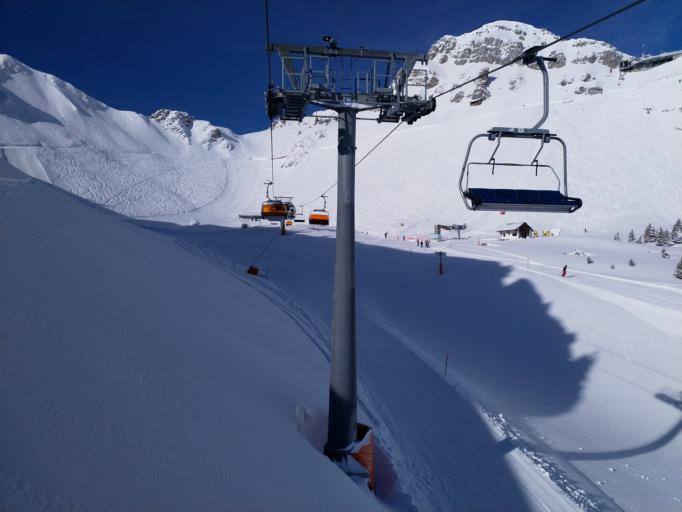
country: CH
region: Bern
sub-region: Obersimmental-Saanen District
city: Saanen
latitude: 46.4569
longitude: 7.2089
